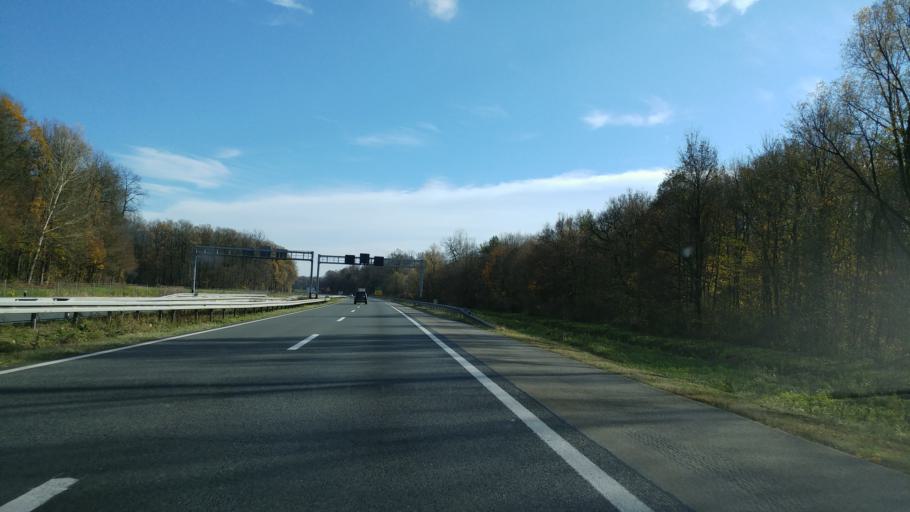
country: HR
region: Sisacko-Moslavacka
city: Novska
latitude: 45.3354
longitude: 16.9288
